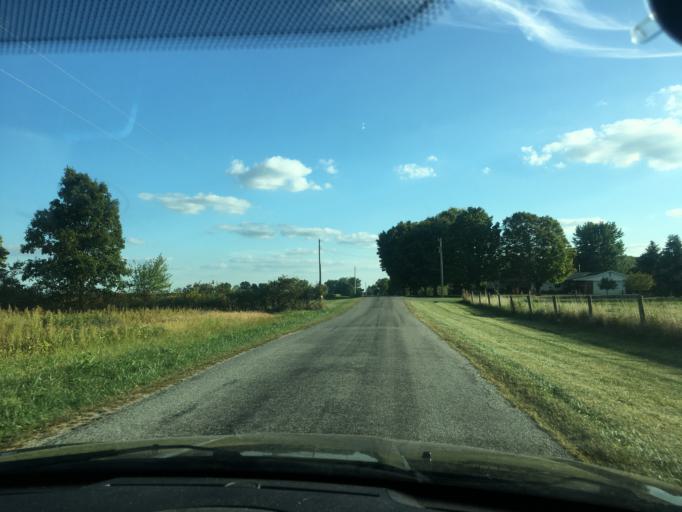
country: US
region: Ohio
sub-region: Champaign County
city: Urbana
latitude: 40.1763
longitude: -83.7633
